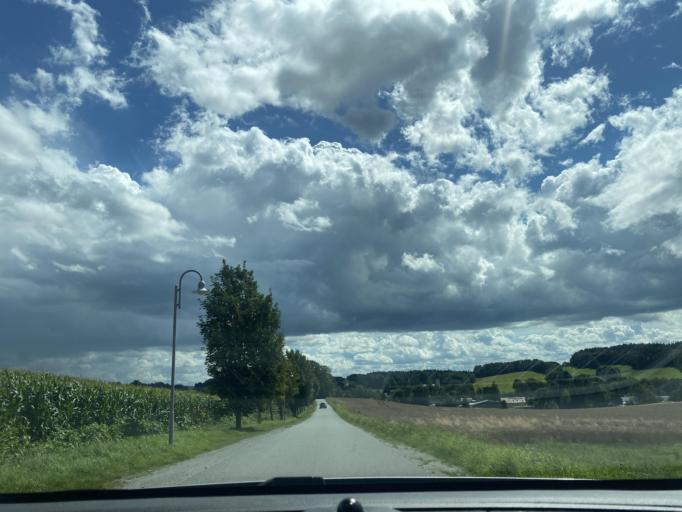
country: DE
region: Saxony
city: Beiersdorf
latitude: 51.0760
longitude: 14.5306
